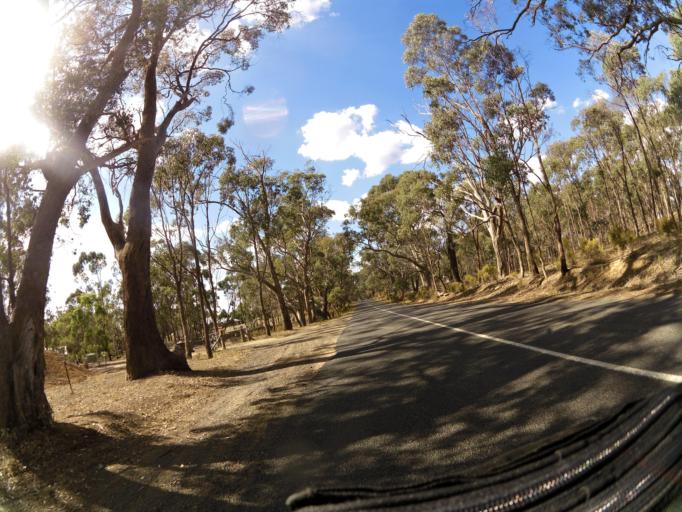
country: AU
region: Victoria
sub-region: Greater Bendigo
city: Kennington
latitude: -36.9536
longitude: 144.7734
